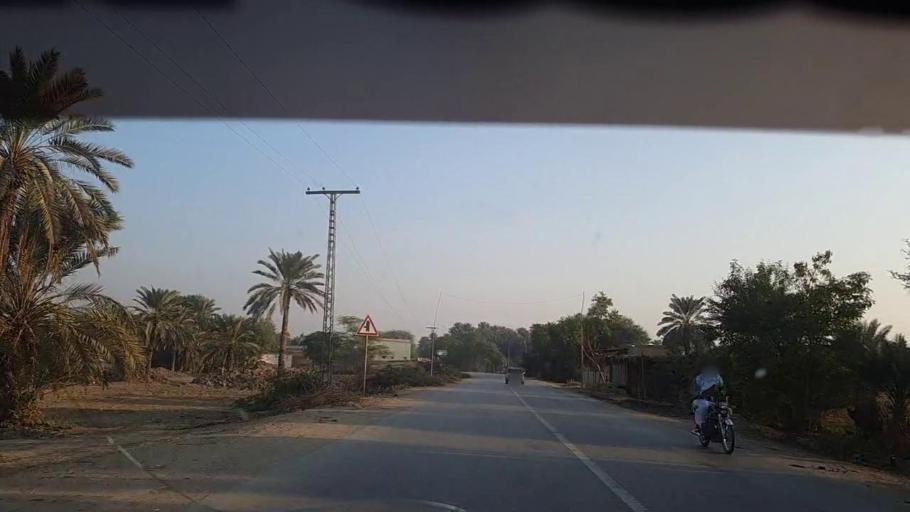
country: PK
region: Sindh
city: Ranipur
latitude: 27.2620
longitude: 68.5250
